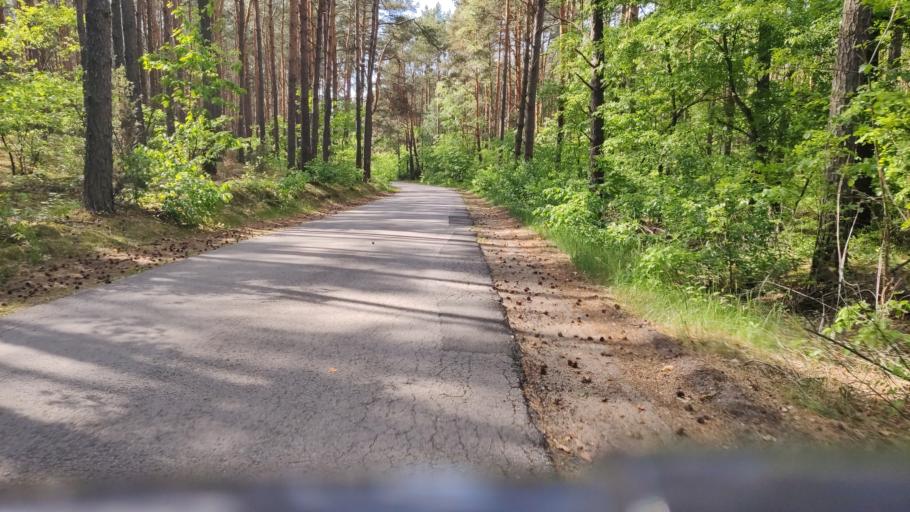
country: PL
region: Kujawsko-Pomorskie
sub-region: Wloclawek
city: Wloclawek
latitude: 52.5965
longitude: 19.0859
